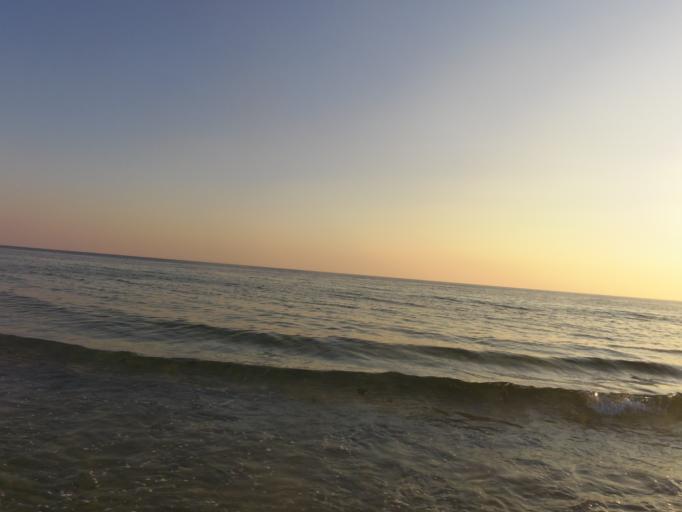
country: US
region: Florida
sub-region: Bay County
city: Laguna Beach
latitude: 30.2181
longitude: -85.8836
